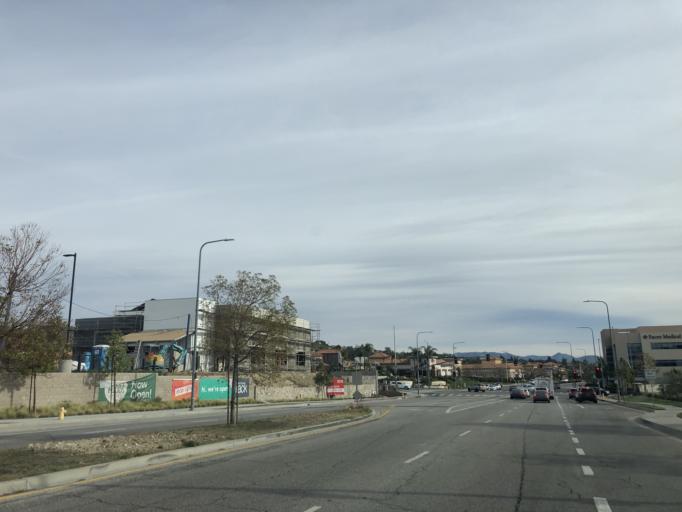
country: US
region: California
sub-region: Los Angeles County
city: Chatsworth
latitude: 34.2753
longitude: -118.5716
